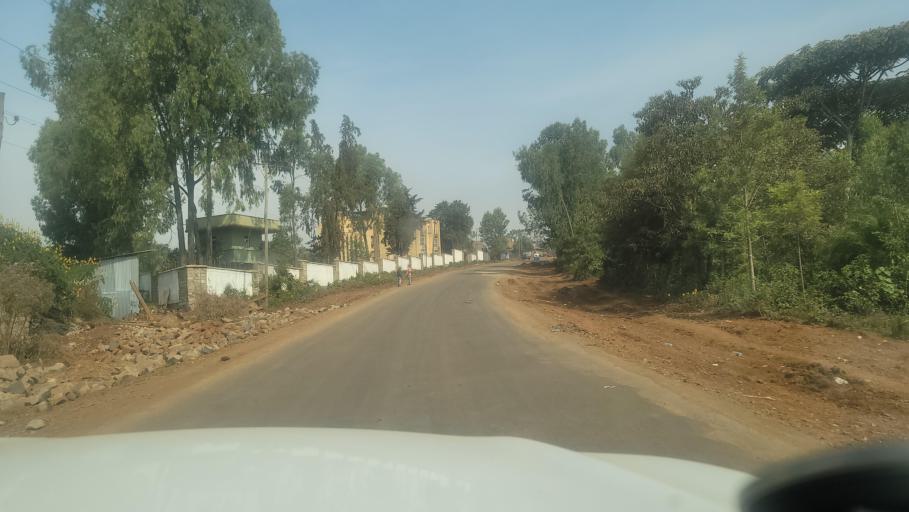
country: ET
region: Oromiya
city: Jima
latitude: 7.7042
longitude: 36.8054
